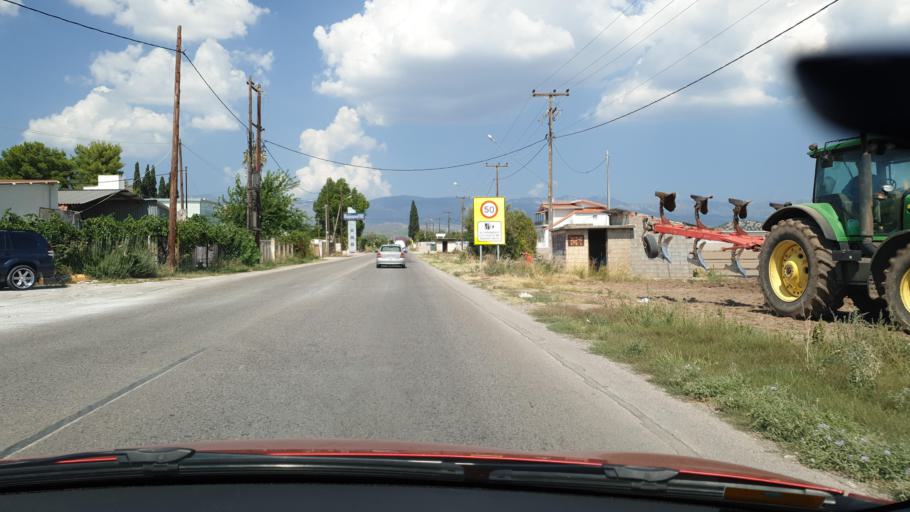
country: GR
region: Central Greece
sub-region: Nomos Evvoias
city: Kastella
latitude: 38.5469
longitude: 23.6287
